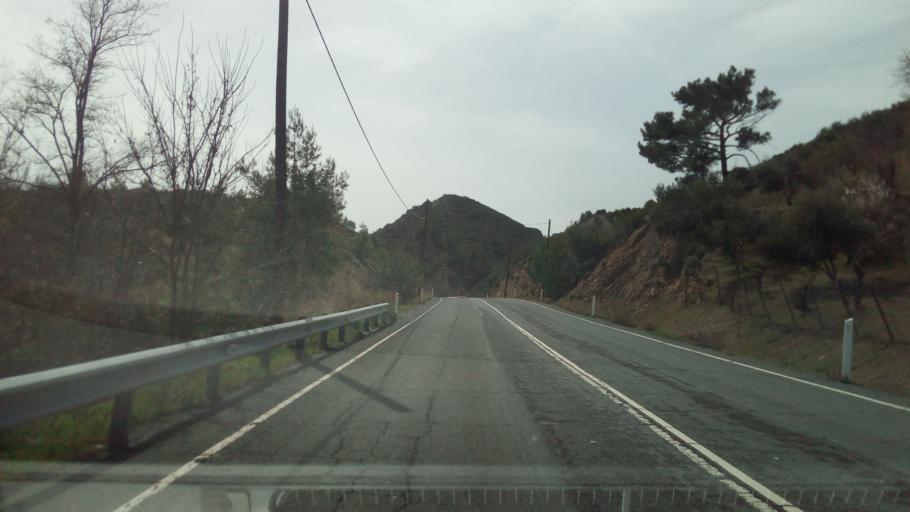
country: CY
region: Limassol
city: Pelendri
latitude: 34.8800
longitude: 32.9460
